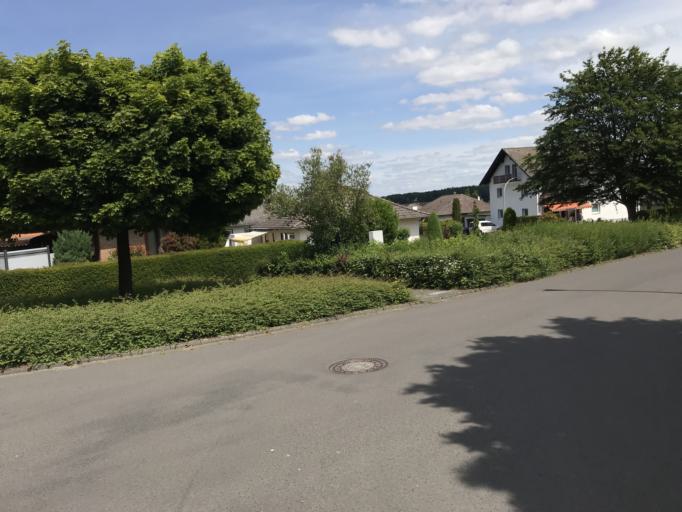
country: DE
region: Hesse
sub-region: Regierungsbezirk Darmstadt
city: Butzbach
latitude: 50.4454
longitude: 8.6511
